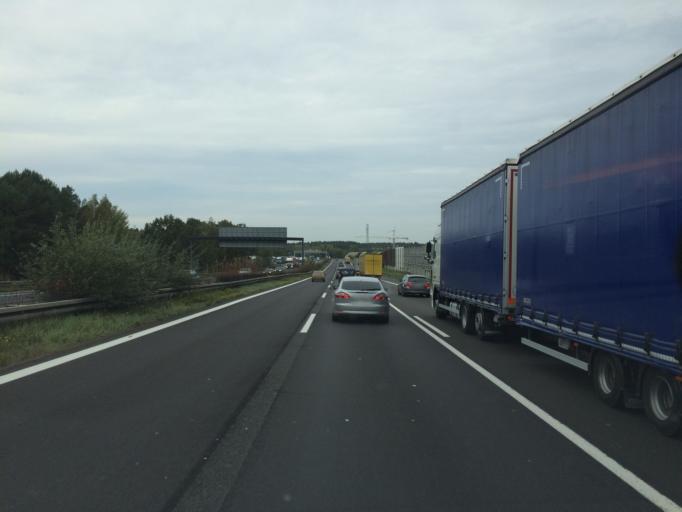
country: DE
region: Brandenburg
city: Michendorf
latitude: 52.3010
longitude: 13.0223
